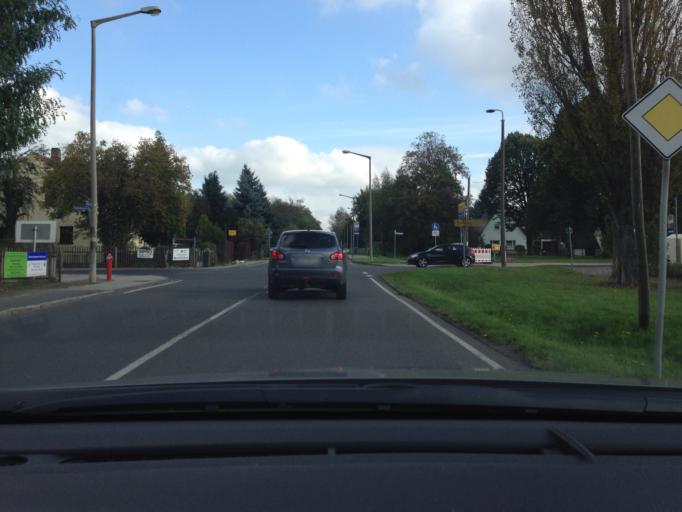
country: DE
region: Saxony
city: Taucha
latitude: 51.3834
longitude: 12.4627
